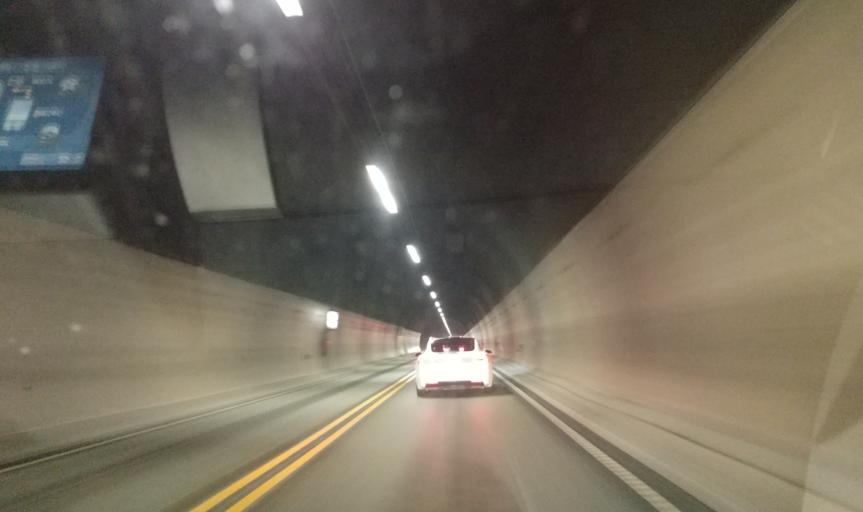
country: NO
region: Sor-Trondelag
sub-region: Malvik
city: Hommelvik
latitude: 63.4229
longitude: 10.8350
